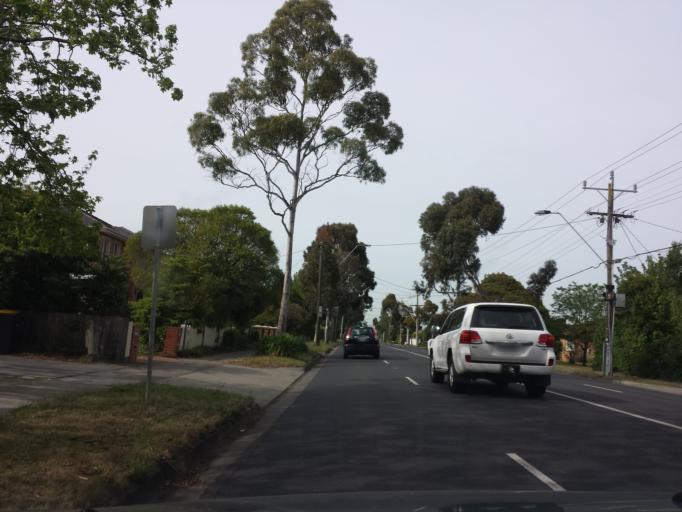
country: AU
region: Victoria
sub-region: Monash
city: Ashwood
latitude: -37.8797
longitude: 145.1283
